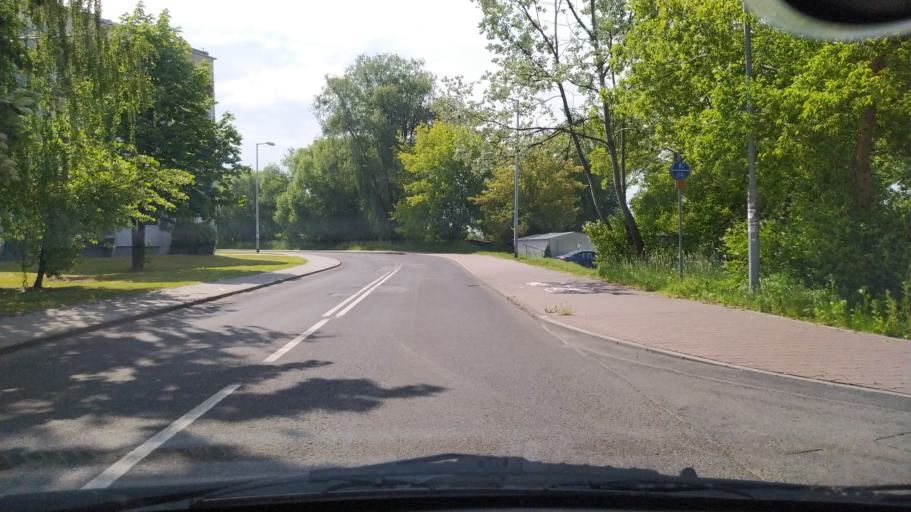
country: PL
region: Silesian Voivodeship
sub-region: Powiat gliwicki
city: Przyszowice
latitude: 50.2848
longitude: 18.7277
